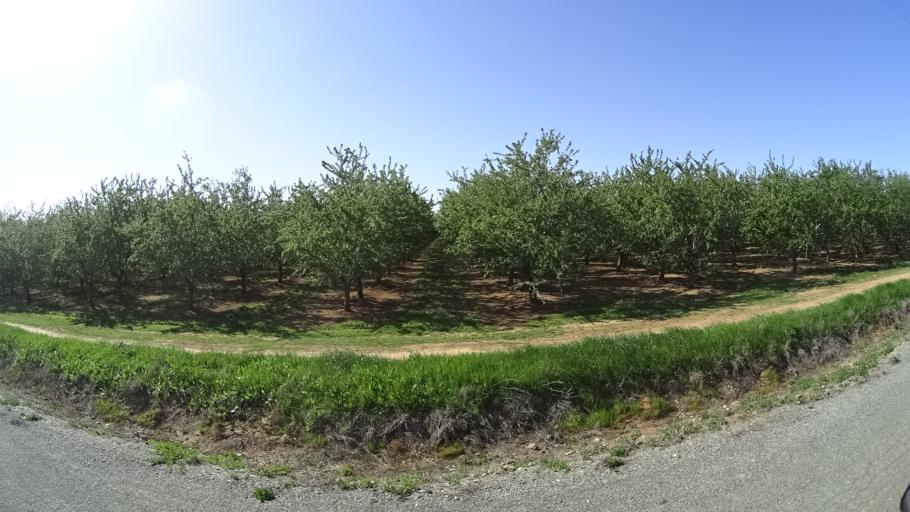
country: US
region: California
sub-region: Glenn County
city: Hamilton City
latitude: 39.7756
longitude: -122.0743
